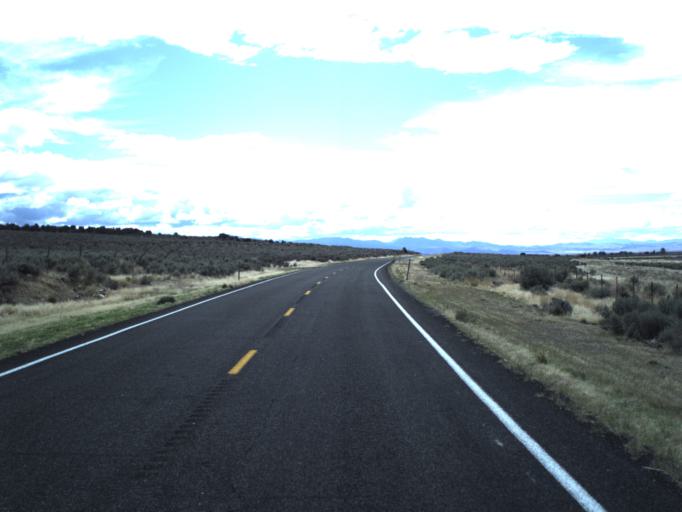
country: US
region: Utah
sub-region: Millard County
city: Fillmore
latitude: 39.0076
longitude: -112.4104
